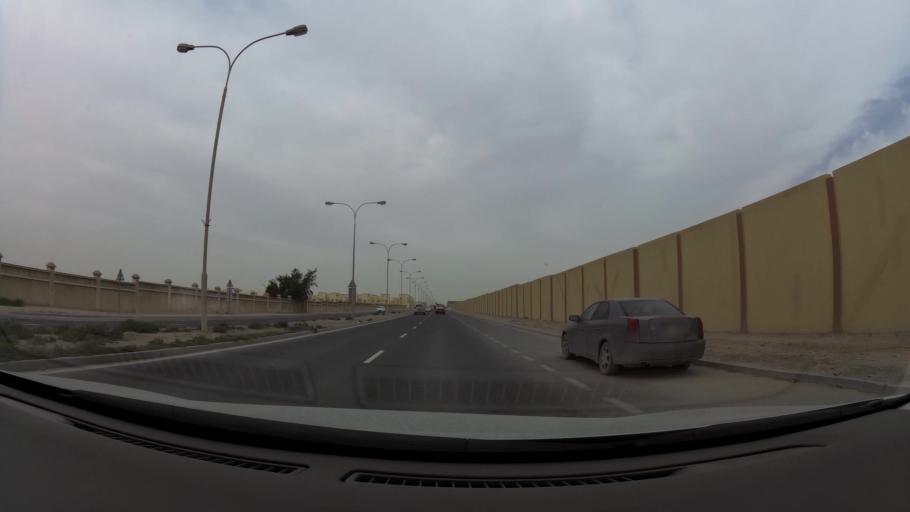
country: QA
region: Baladiyat ar Rayyan
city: Ar Rayyan
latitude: 25.2262
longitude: 51.4497
